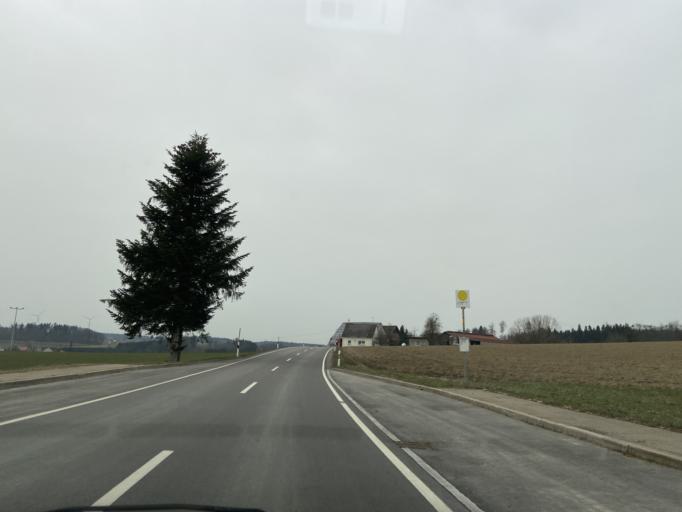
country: DE
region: Baden-Wuerttemberg
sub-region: Tuebingen Region
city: Illmensee
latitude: 47.8742
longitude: 9.3571
